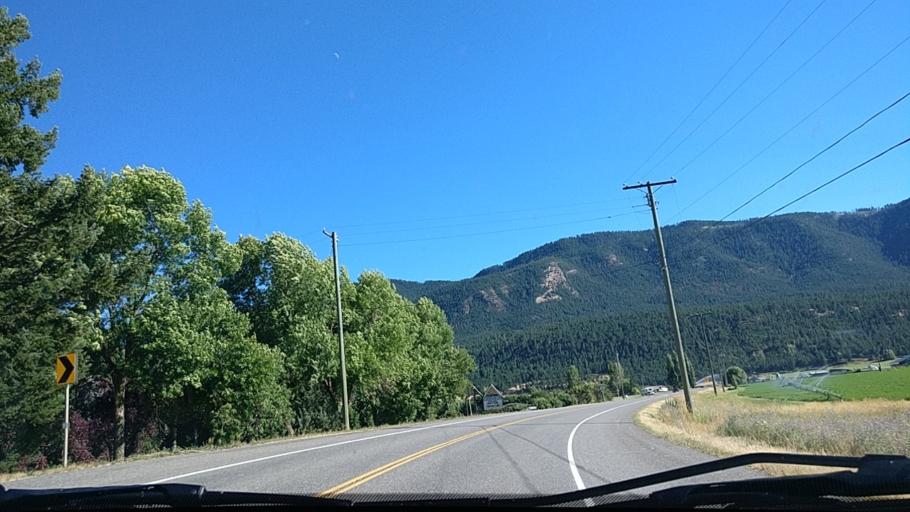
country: CA
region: British Columbia
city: Chase
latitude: 50.4655
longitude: -119.7384
